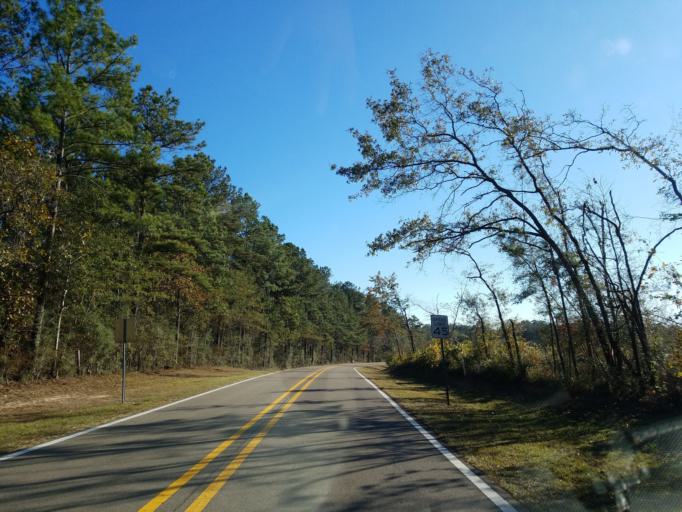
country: US
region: Mississippi
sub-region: Forrest County
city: Hattiesburg
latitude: 31.2550
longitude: -89.2938
